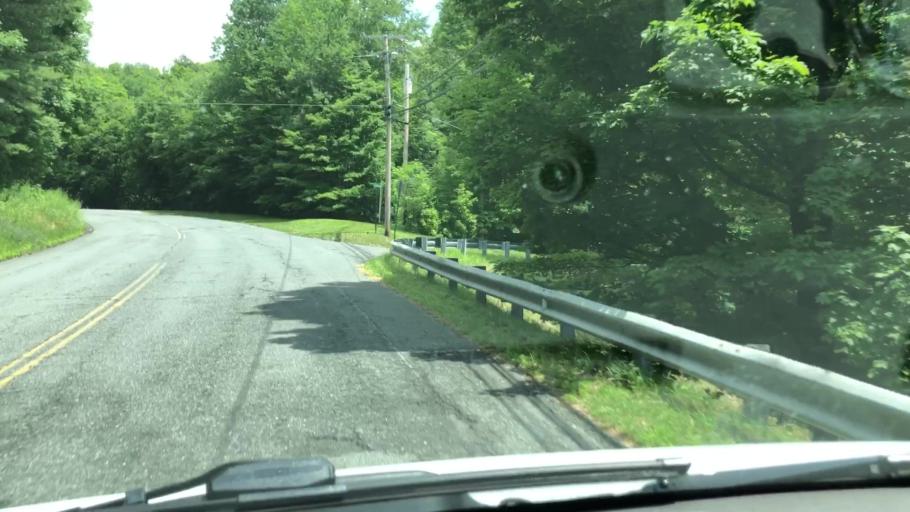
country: US
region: Massachusetts
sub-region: Berkshire County
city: Adams
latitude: 42.5798
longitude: -73.0936
